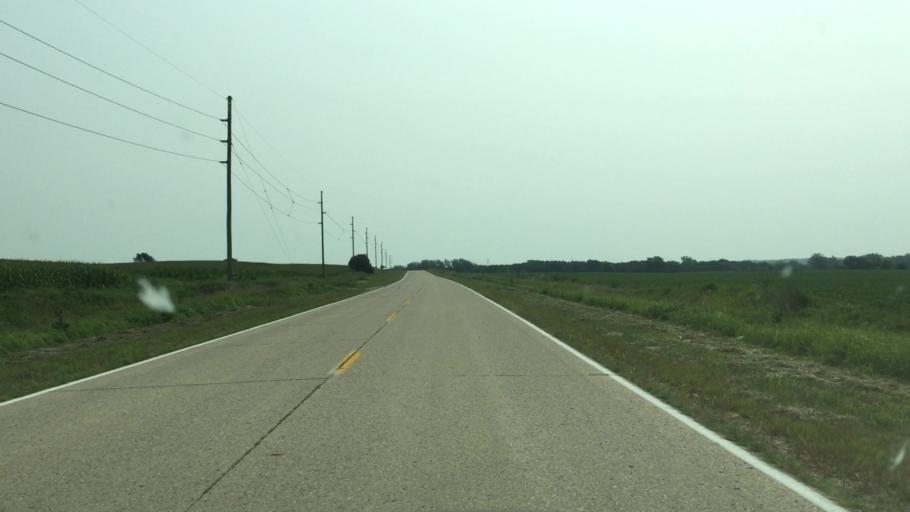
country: US
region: Iowa
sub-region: Dickinson County
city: Milford
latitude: 43.3714
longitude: -95.1912
